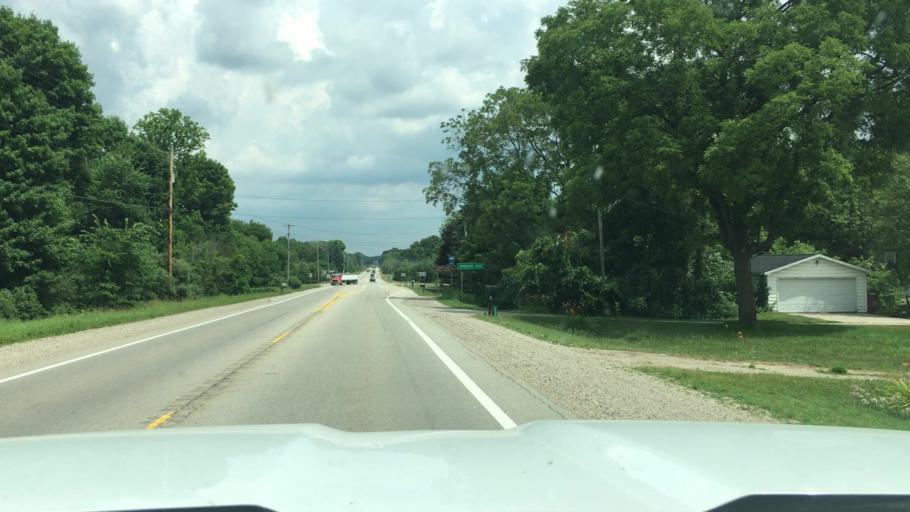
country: US
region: Michigan
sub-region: Montcalm County
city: Greenville
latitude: 43.1764
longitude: -85.3952
